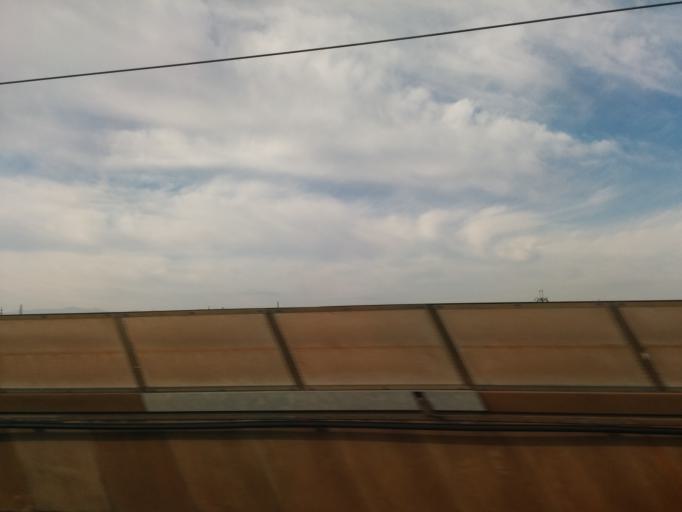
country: JP
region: Shiga Prefecture
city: Omihachiman
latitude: 35.1126
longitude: 136.1170
